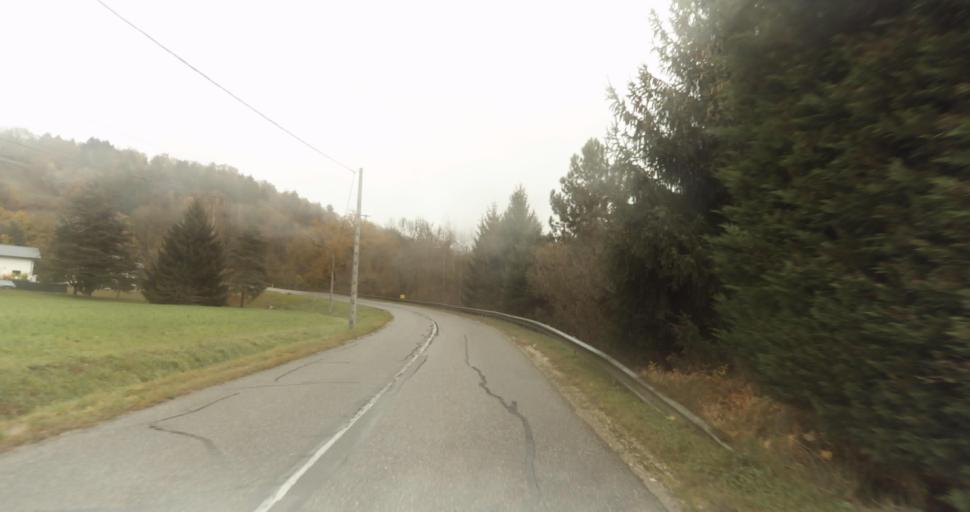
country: FR
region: Rhone-Alpes
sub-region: Departement de la Haute-Savoie
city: Villaz
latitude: 45.9386
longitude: 6.1683
